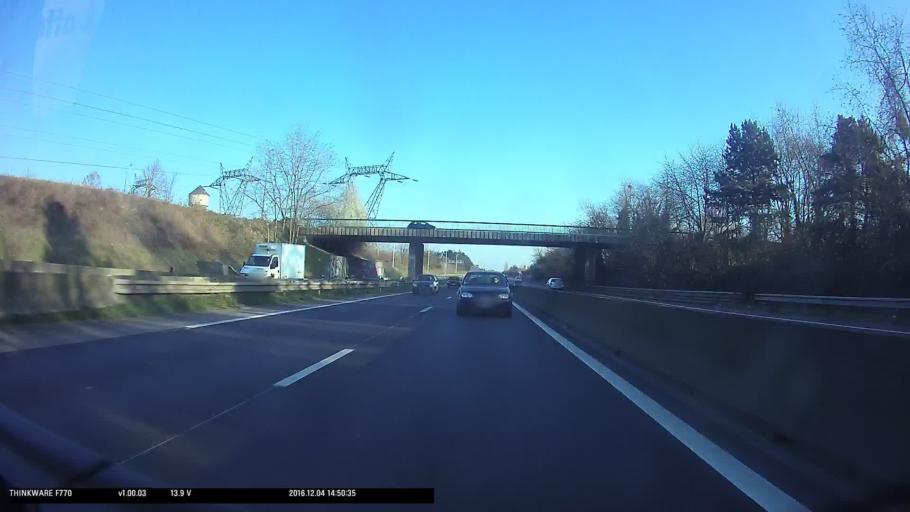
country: FR
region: Ile-de-France
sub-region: Departement du Val-d'Oise
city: Osny
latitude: 49.0563
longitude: 2.0463
